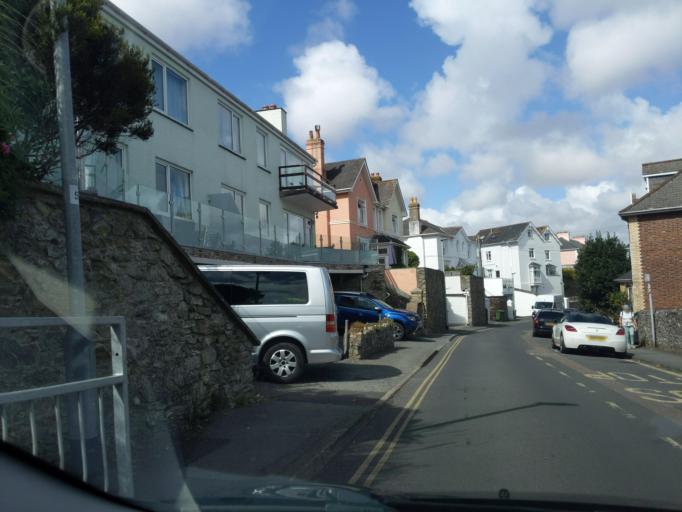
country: GB
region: England
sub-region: Devon
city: Salcombe
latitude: 50.2375
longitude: -3.7697
